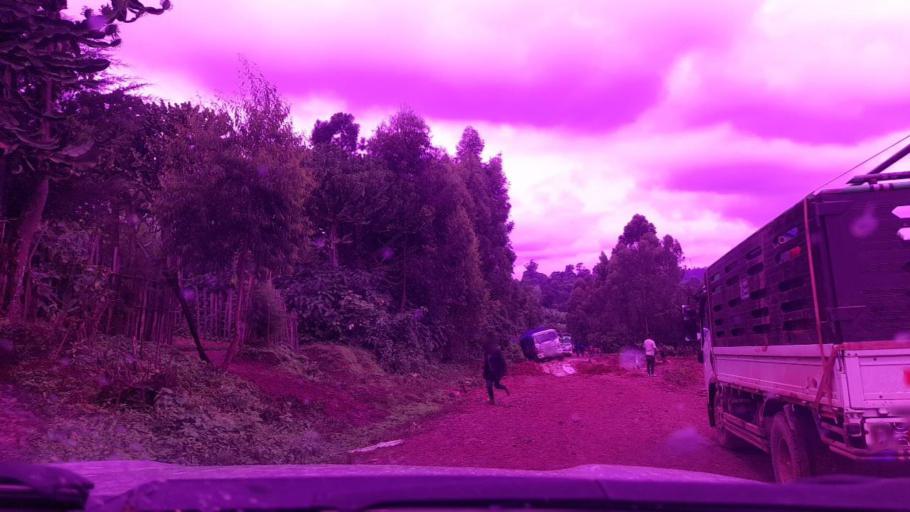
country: ET
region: Southern Nations, Nationalities, and People's Region
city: Tippi
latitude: 7.5658
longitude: 35.7895
